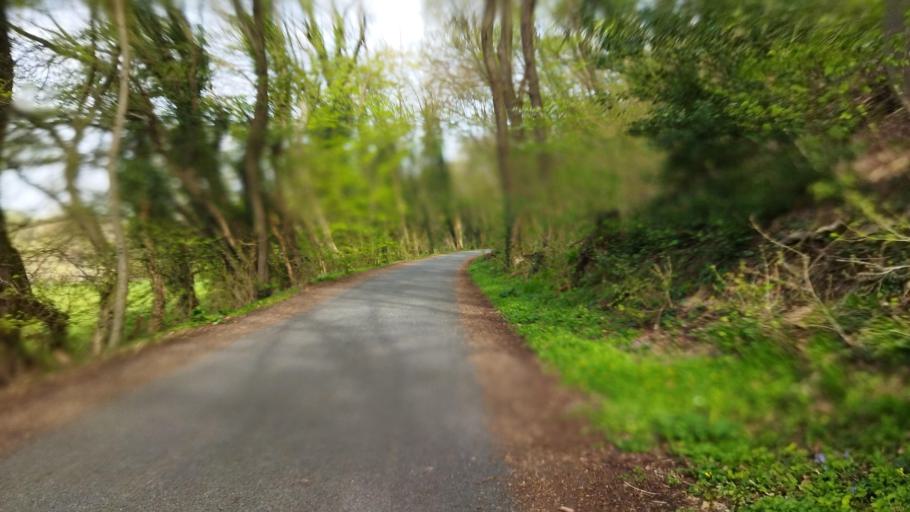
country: DE
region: North Rhine-Westphalia
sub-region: Regierungsbezirk Detmold
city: Vlotho
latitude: 52.1970
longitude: 8.8640
